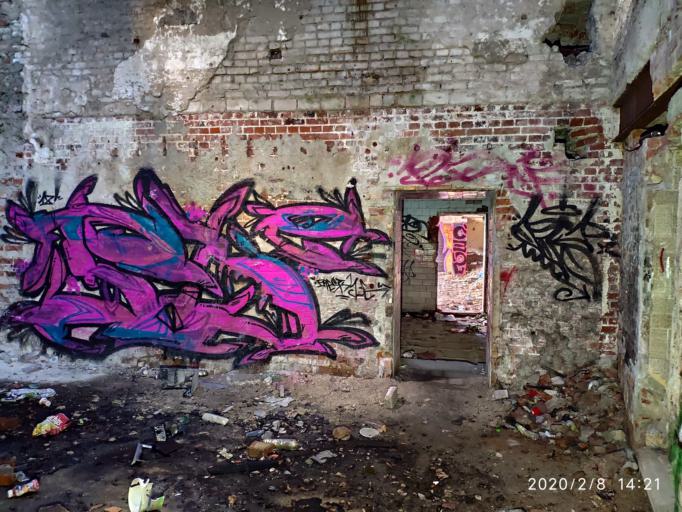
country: PL
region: Lubusz
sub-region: Powiat nowosolski
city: Nowa Sol
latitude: 51.7980
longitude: 15.7182
